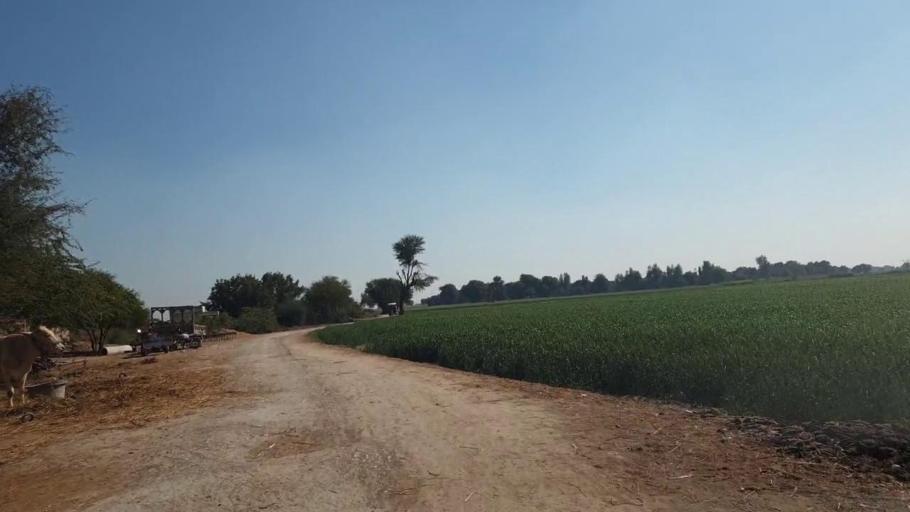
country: PK
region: Sindh
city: Shahpur Chakar
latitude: 26.1252
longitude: 68.6401
